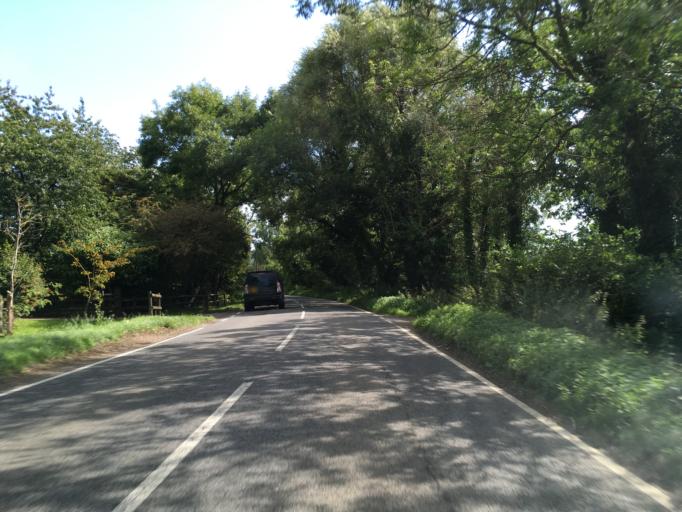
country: GB
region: England
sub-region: Gloucestershire
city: Stonehouse
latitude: 51.7347
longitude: -2.3189
